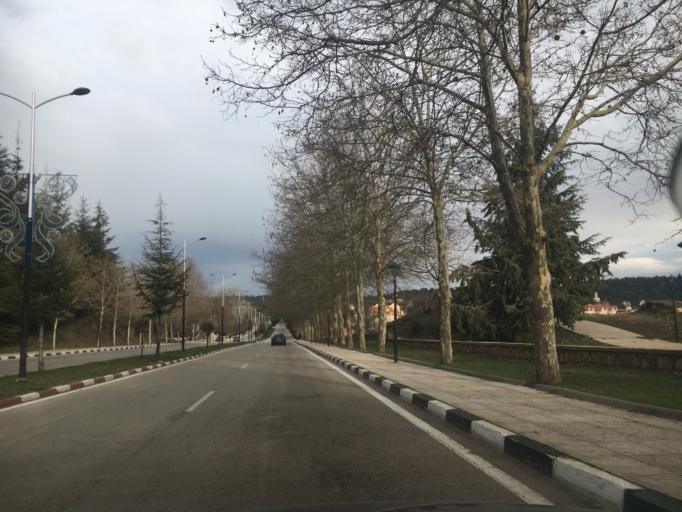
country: MA
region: Meknes-Tafilalet
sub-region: Ifrane
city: Ifrane
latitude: 33.5277
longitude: -5.1231
